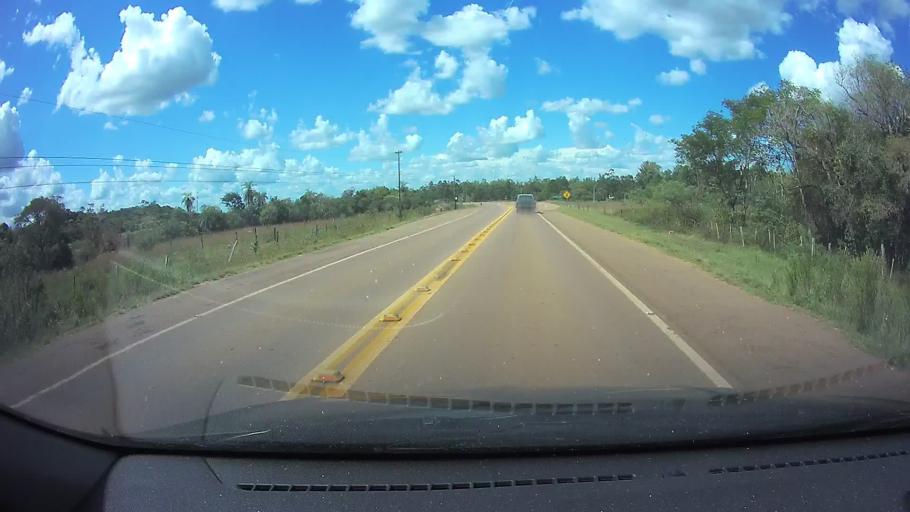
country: PY
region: Guaira
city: Itape
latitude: -25.9114
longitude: -56.6770
